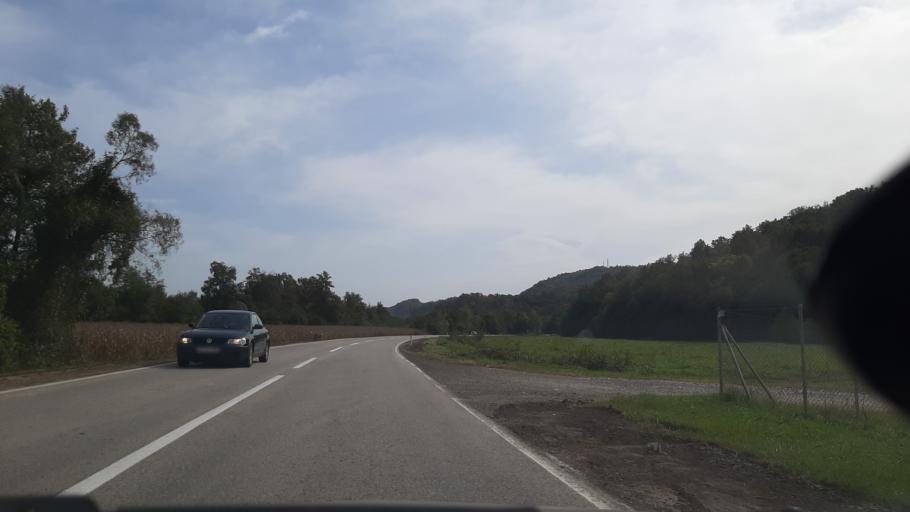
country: BA
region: Republika Srpska
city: Maglajani
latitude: 44.8765
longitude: 17.3815
